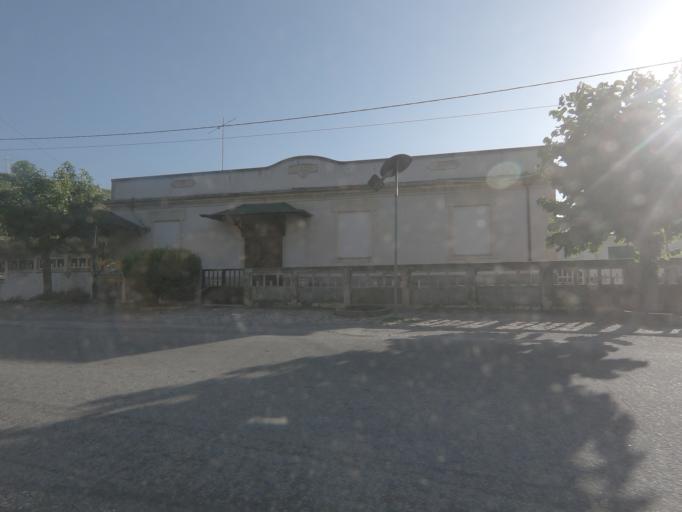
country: PT
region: Viseu
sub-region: Tabuaco
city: Tabuaco
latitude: 41.1749
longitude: -7.5530
